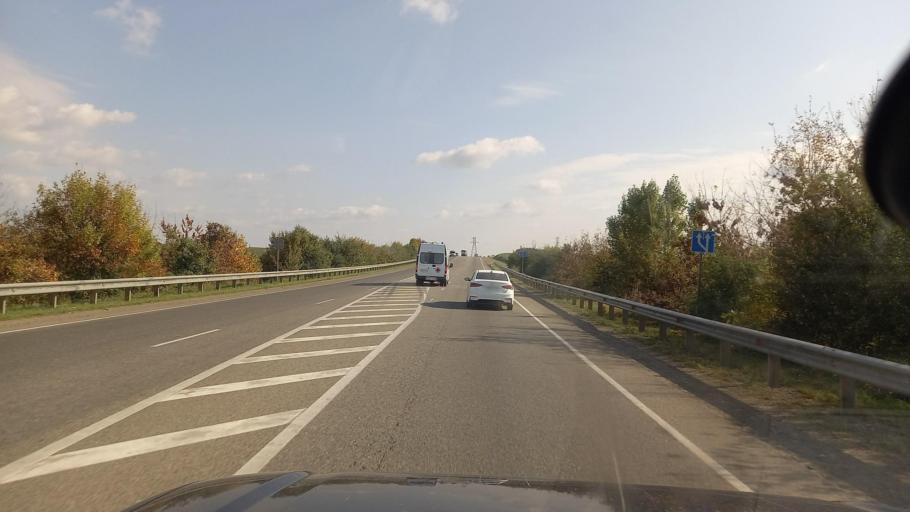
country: RU
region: Krasnodarskiy
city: Akhtyrskiy
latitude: 44.8544
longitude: 38.3443
